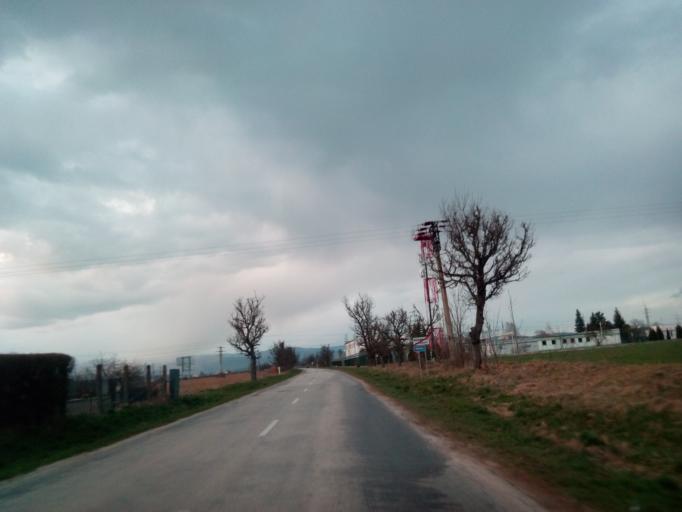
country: SK
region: Kosicky
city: Moldava nad Bodvou
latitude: 48.5916
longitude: 20.9953
